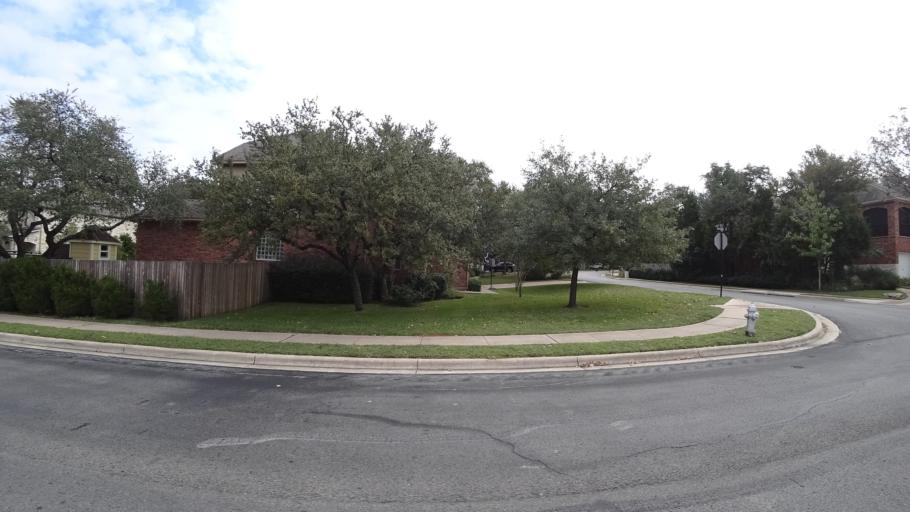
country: US
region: Texas
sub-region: Travis County
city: Shady Hollow
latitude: 30.1894
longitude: -97.9038
